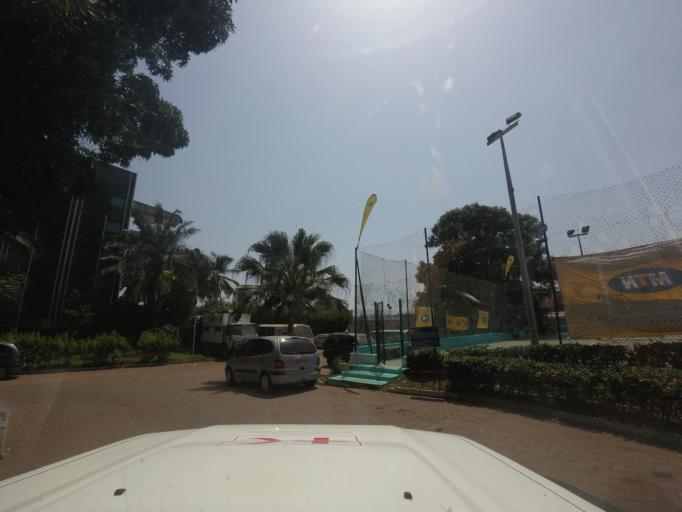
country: GN
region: Conakry
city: Camayenne
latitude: 9.5067
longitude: -13.7194
